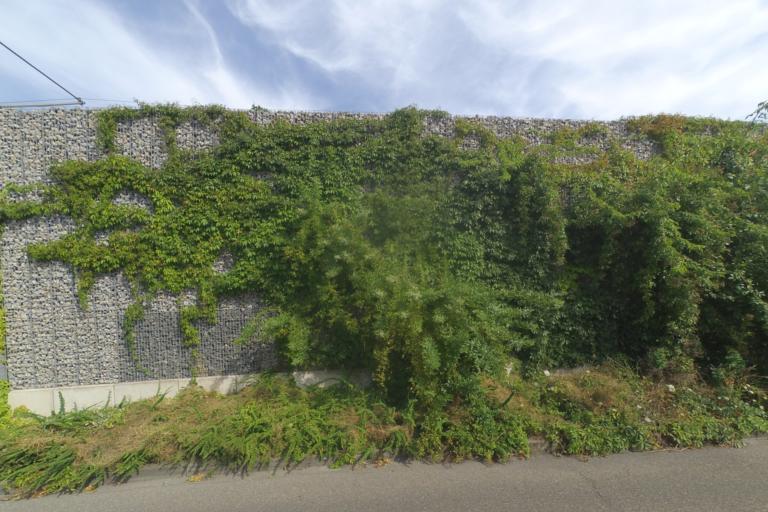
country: DE
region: Rheinland-Pfalz
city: Limburgerhof
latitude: 49.4179
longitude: 8.3853
